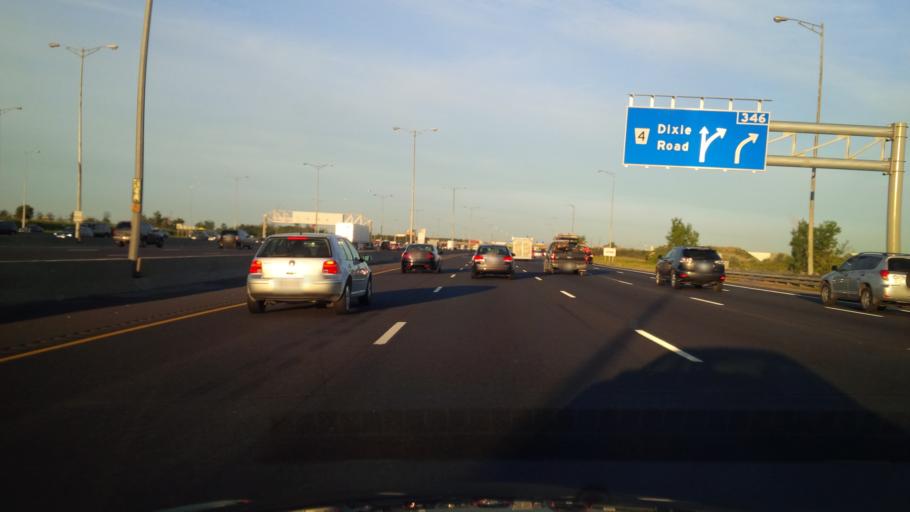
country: CA
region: Ontario
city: Etobicoke
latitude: 43.6527
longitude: -79.6275
